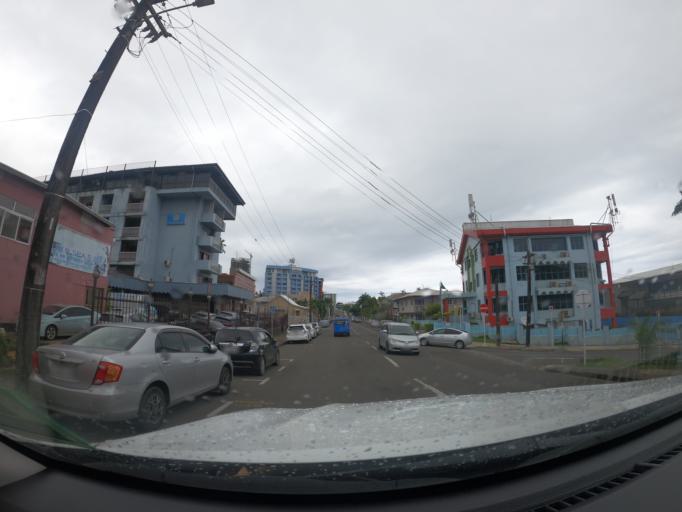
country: FJ
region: Central
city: Suva
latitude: -18.1426
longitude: 178.4252
